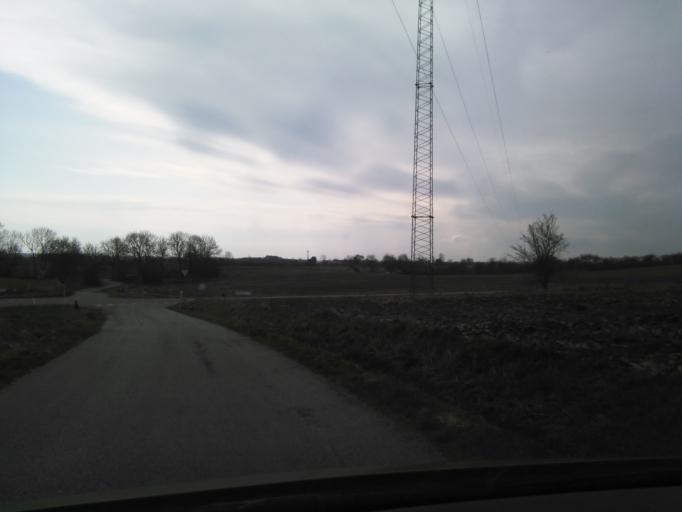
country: DK
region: Central Jutland
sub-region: Arhus Kommune
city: Malling
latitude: 56.0257
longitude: 10.2164
